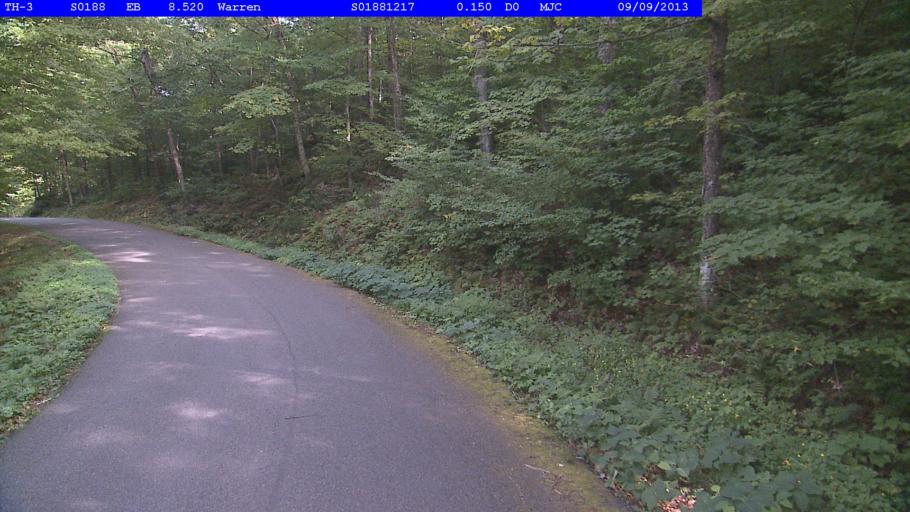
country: US
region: Vermont
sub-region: Addison County
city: Bristol
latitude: 44.0945
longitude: -72.9197
